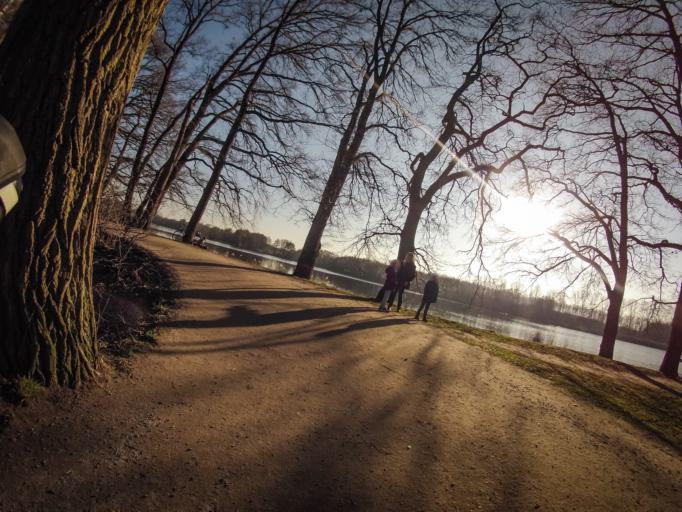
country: DE
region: Lower Saxony
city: Osnabrueck
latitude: 52.2889
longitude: 7.9885
